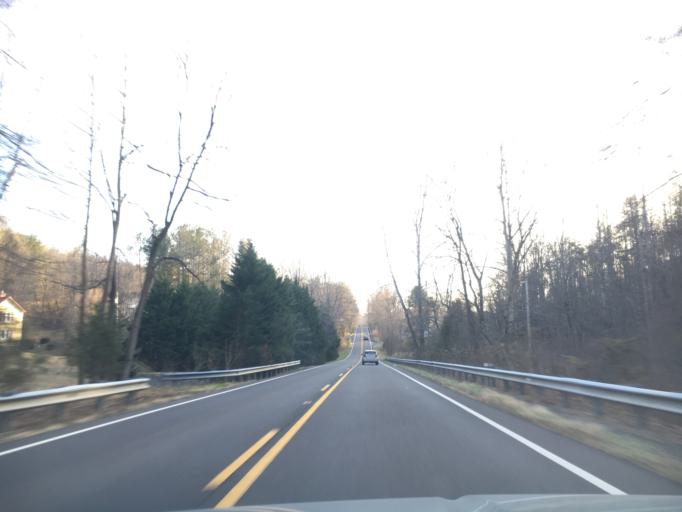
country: US
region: Virginia
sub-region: Culpeper County
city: Merrimac
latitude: 38.5688
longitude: -78.1587
